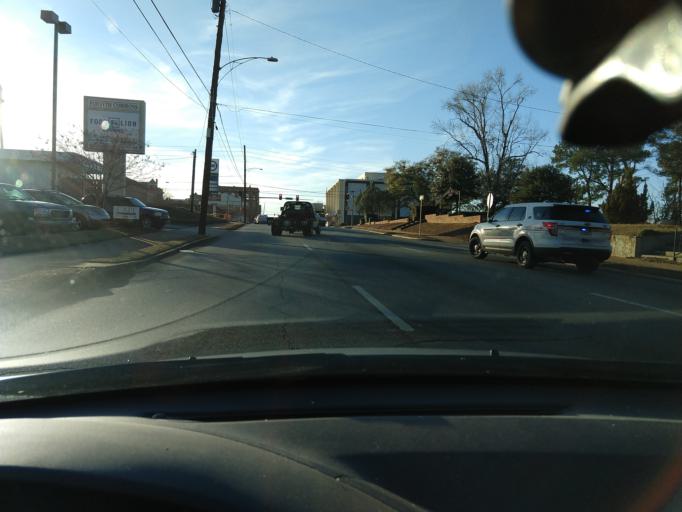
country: US
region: Georgia
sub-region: Sumter County
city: Americus
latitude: 32.0733
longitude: -84.2295
